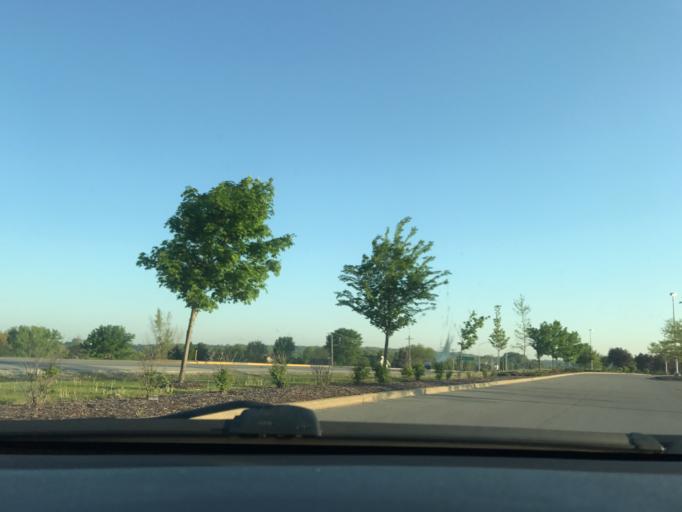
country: US
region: Illinois
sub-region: Kane County
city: South Elgin
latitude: 42.0117
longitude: -88.3361
